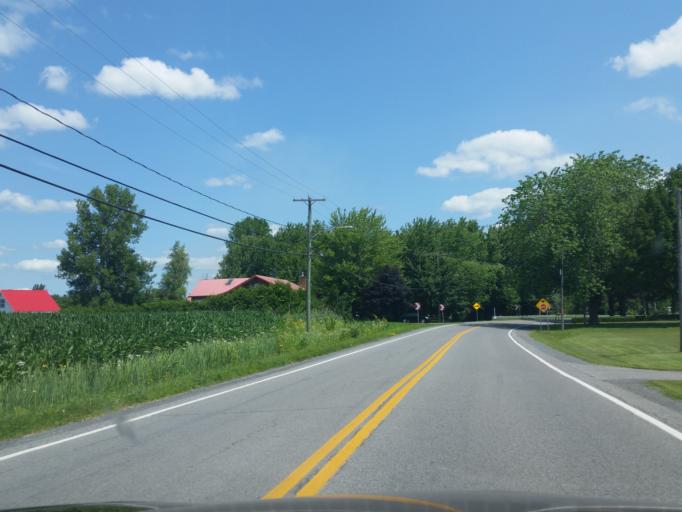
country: CA
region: Quebec
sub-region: Monteregie
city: Richelieu
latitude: 45.4074
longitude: -73.2557
